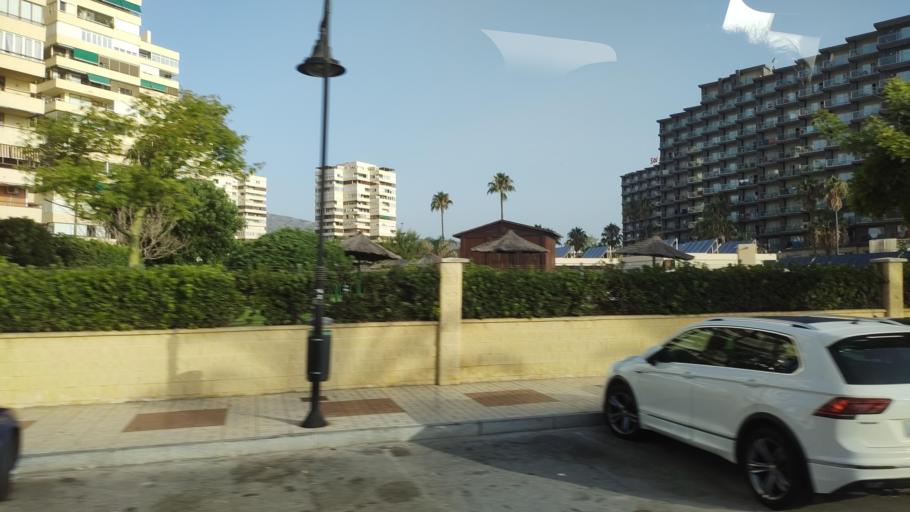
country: ES
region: Andalusia
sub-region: Provincia de Malaga
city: Torremolinos
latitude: 36.6302
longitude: -4.4897
